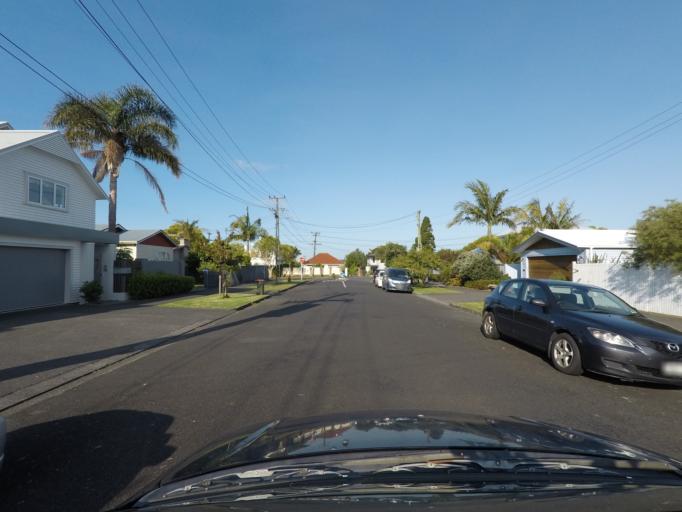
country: NZ
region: Auckland
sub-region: Auckland
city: Rosebank
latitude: -36.8597
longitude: 174.7053
